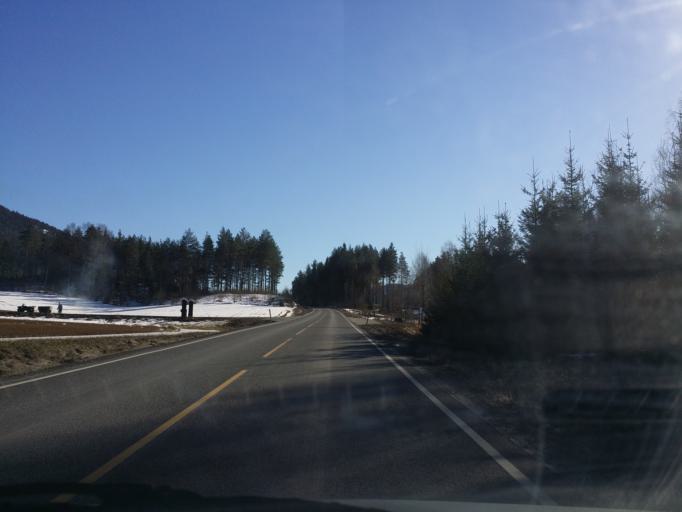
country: NO
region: Buskerud
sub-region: Ringerike
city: Honefoss
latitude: 60.3498
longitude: 10.1031
